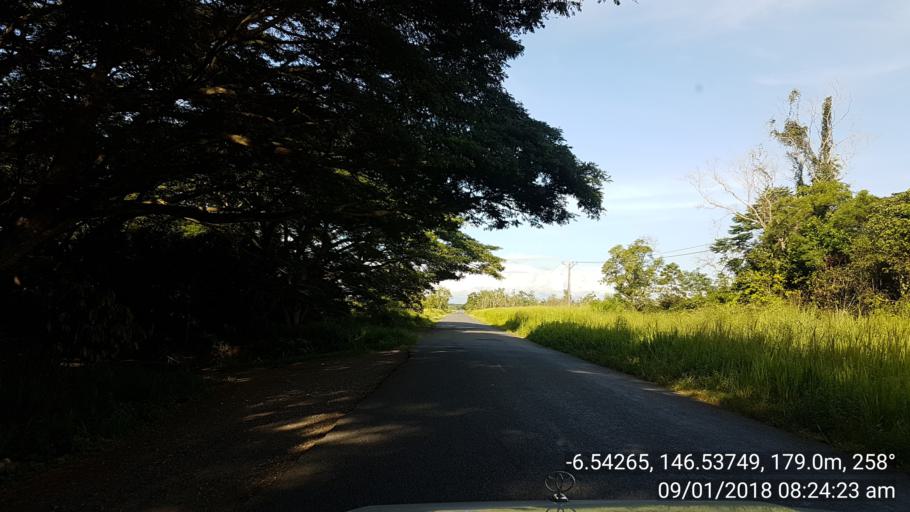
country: PG
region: Morobe
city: Lae
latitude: -6.5427
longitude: 146.5375
